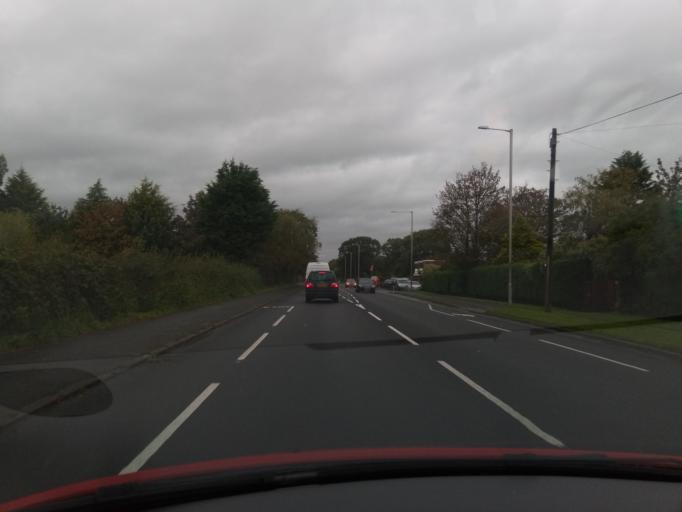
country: GB
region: England
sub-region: Lancashire
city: Catterall
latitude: 53.8259
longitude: -2.7362
